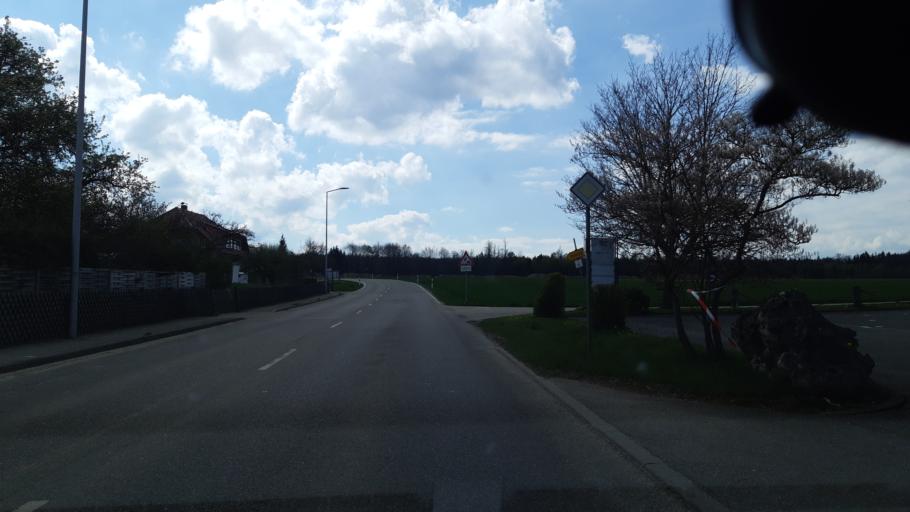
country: DE
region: Baden-Wuerttemberg
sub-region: Regierungsbezirk Stuttgart
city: Westhausen
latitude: 48.8045
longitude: 10.1817
